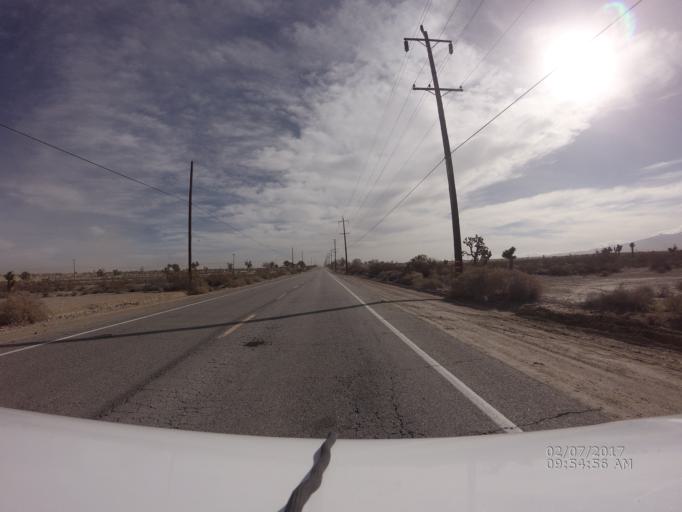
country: US
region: California
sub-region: Los Angeles County
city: Lake Los Angeles
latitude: 34.5800
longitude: -117.8004
